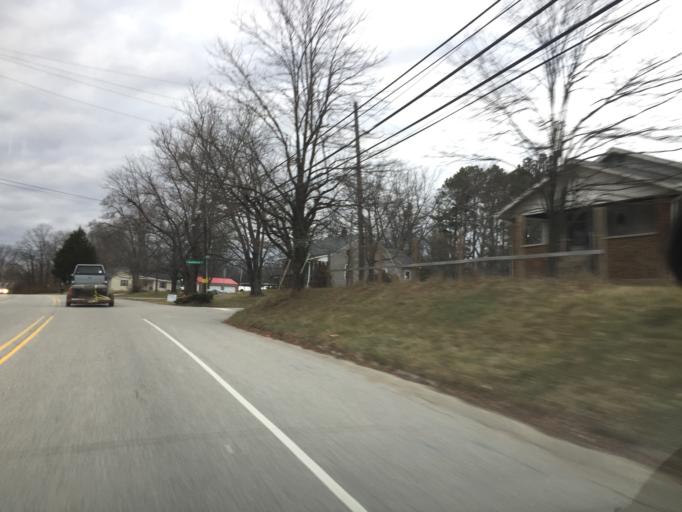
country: US
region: Indiana
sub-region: Monroe County
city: Ellettsville
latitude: 39.2076
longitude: -86.5733
